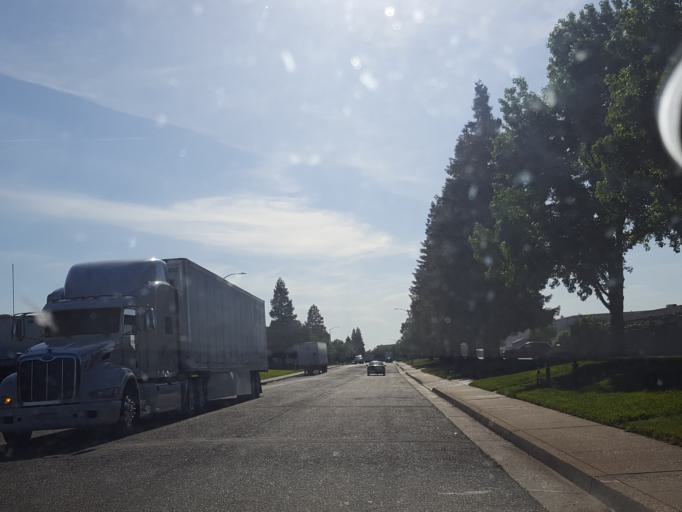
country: US
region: California
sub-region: Sacramento County
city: Florin
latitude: 38.5047
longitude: -121.3912
